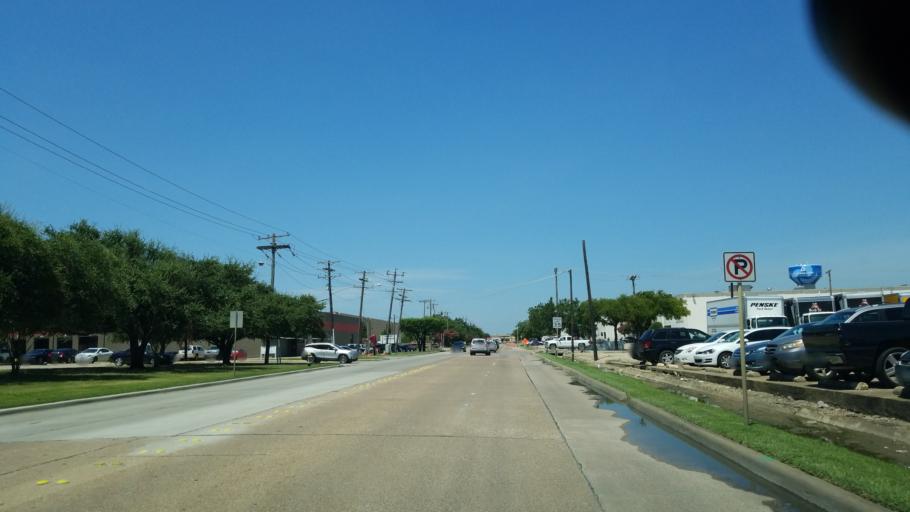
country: US
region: Texas
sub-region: Dallas County
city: Carrollton
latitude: 32.9466
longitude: -96.9106
